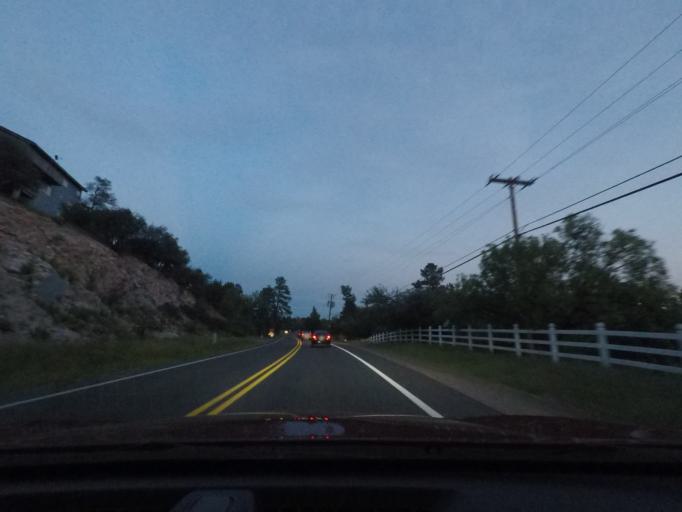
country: US
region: Arizona
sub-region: Yavapai County
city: Prescott
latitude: 34.5728
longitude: -112.5127
